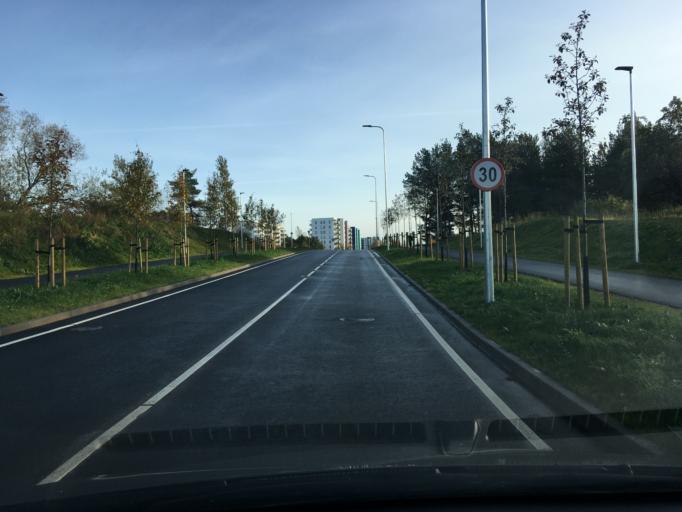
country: EE
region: Harju
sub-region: Viimsi vald
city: Viimsi
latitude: 59.4500
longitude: 24.8211
